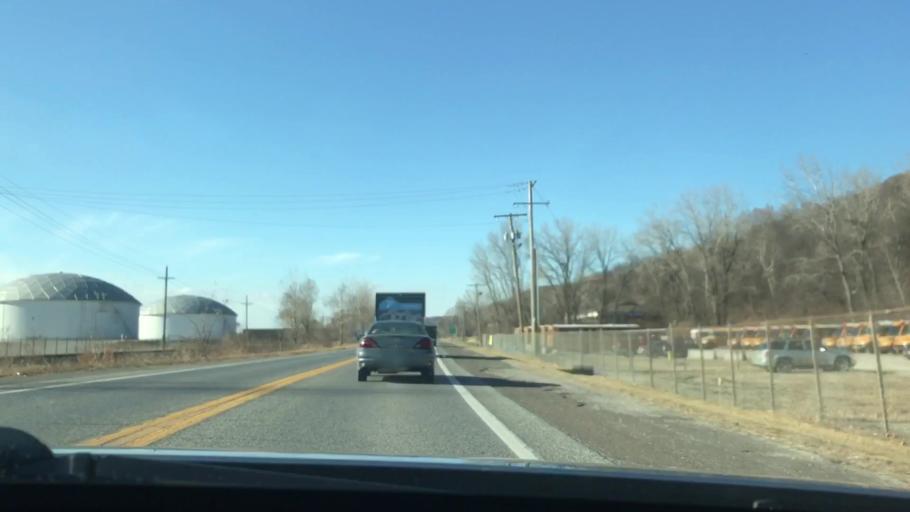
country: US
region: Missouri
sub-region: Platte County
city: Parkville
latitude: 39.1798
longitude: -94.6578
